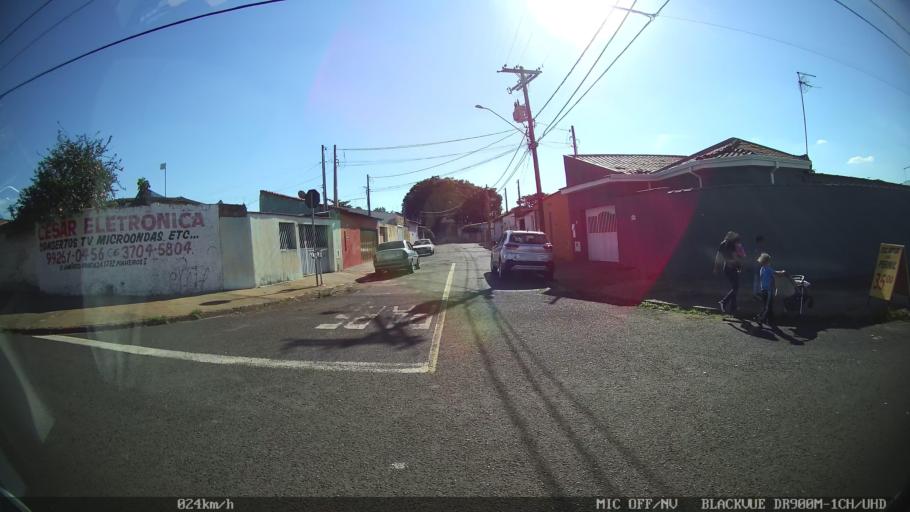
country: BR
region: Sao Paulo
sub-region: Franca
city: Franca
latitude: -20.4962
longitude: -47.4149
